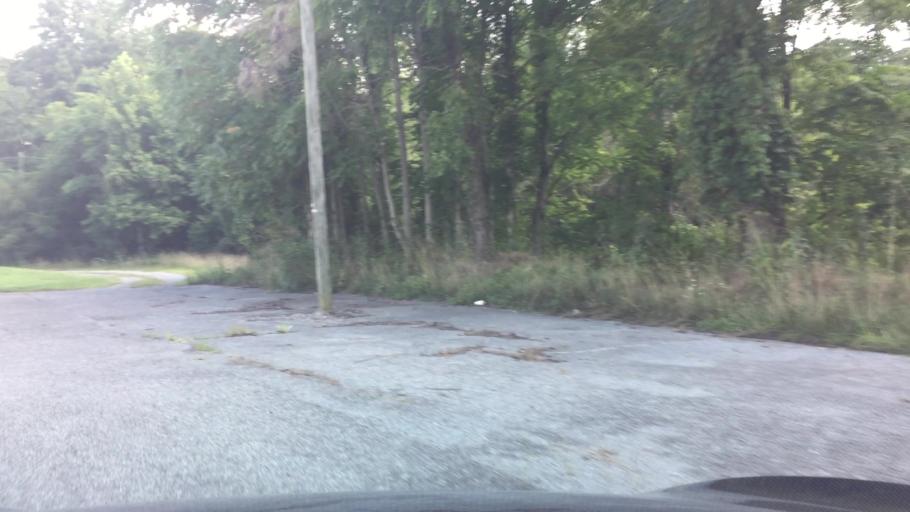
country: US
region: Virginia
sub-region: Wythe County
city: Wytheville
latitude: 36.9441
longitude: -81.0472
